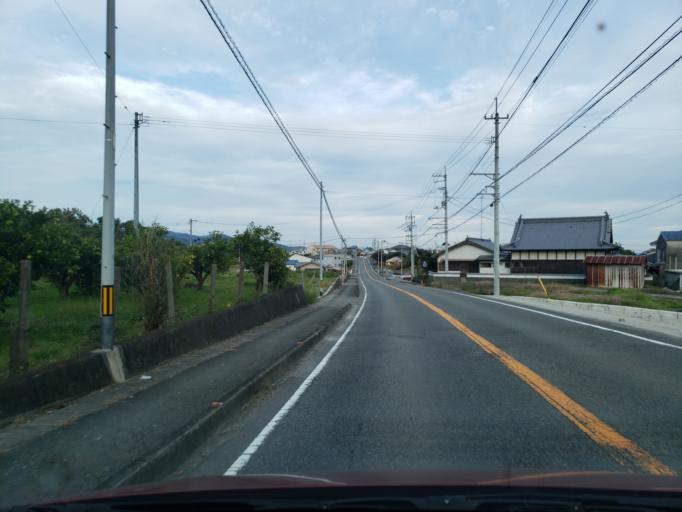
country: JP
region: Tokushima
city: Kamojimacho-jogejima
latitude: 34.0791
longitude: 134.2529
